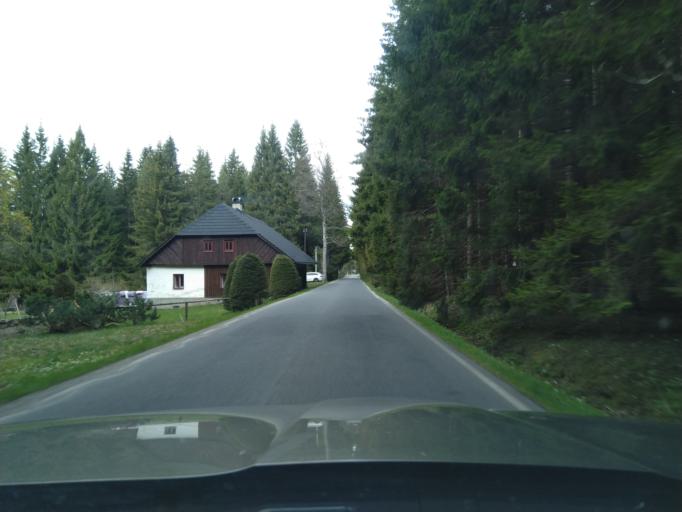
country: CZ
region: Jihocesky
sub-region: Okres Prachatice
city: Borova Lada
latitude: 49.0189
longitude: 13.6665
